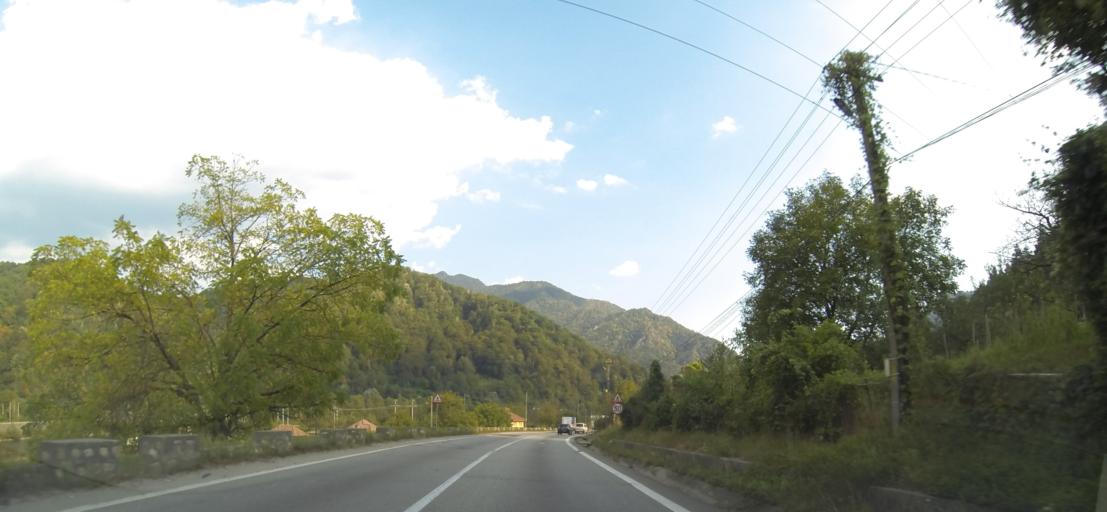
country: RO
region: Valcea
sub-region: Comuna Brezoi
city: Brezoi
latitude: 45.3438
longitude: 24.2746
